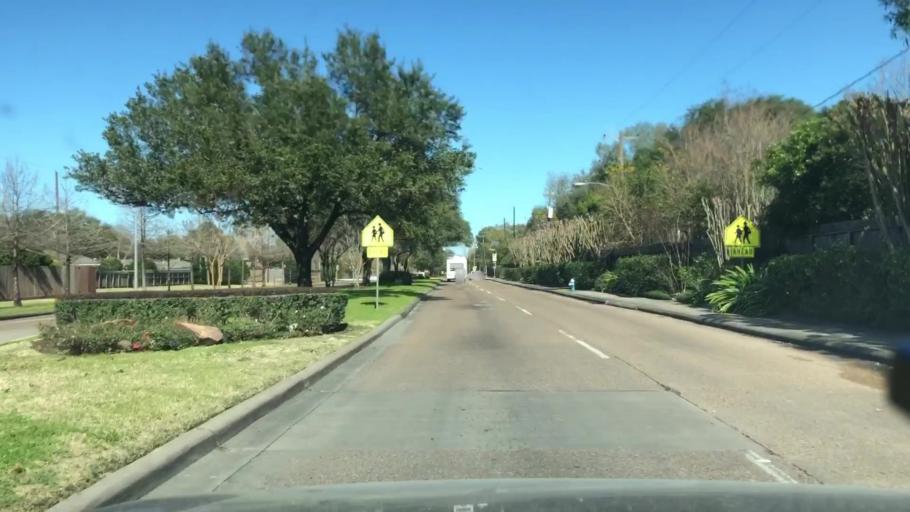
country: US
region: Texas
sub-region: Harris County
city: Bellaire
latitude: 29.6797
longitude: -95.4928
